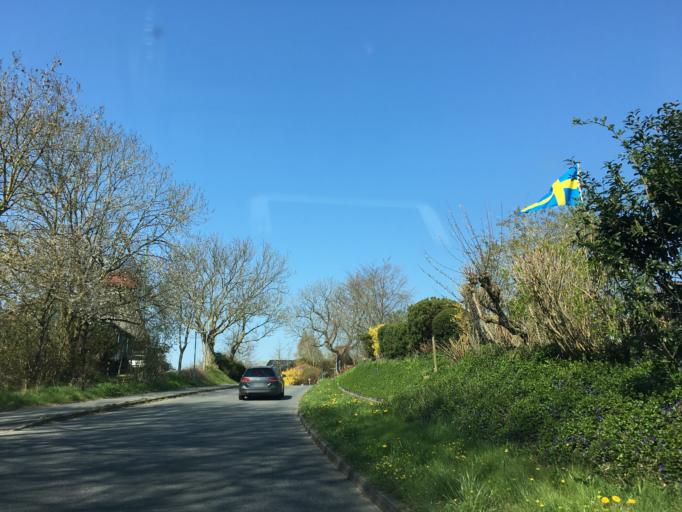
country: DE
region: Schleswig-Holstein
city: Dollrottfeld
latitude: 54.5918
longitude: 9.8036
